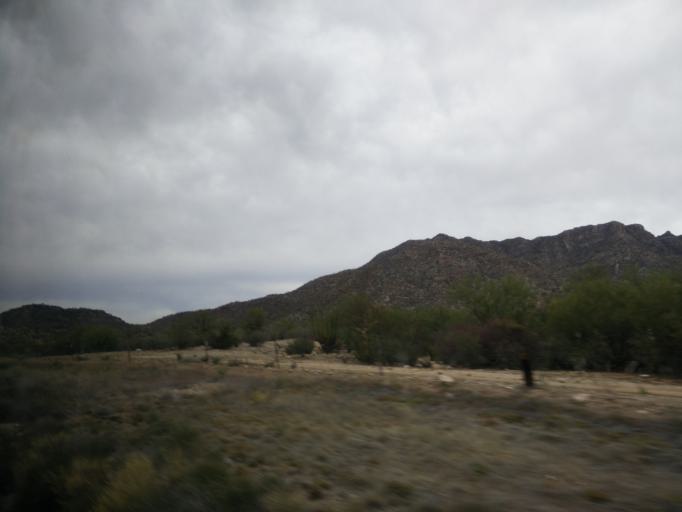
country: MX
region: Sonora
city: Hermosillo
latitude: 28.9725
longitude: -110.9639
